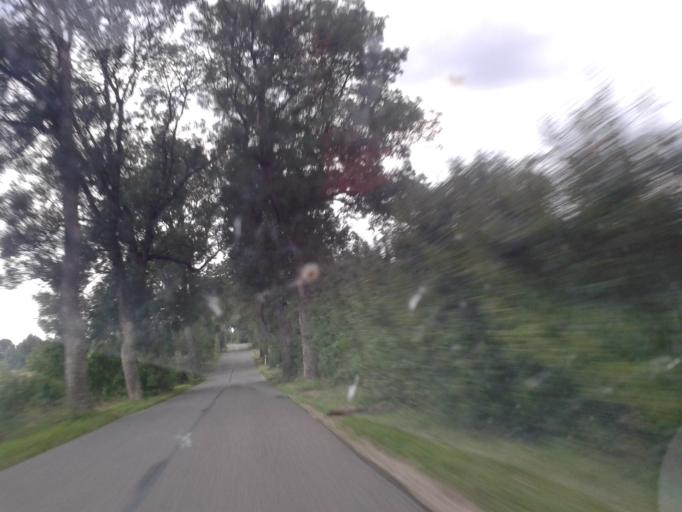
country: PL
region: West Pomeranian Voivodeship
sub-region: Powiat koszalinski
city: Bobolice
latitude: 53.8982
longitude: 16.5284
